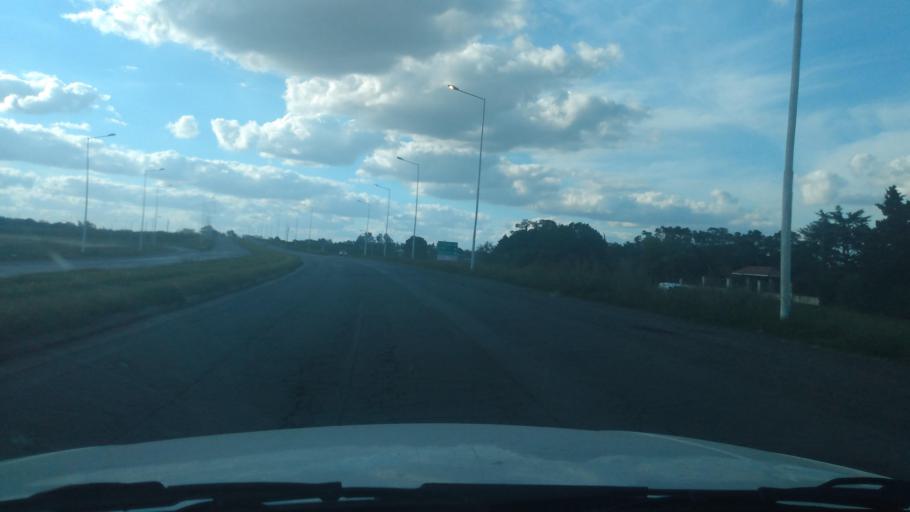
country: AR
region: Buenos Aires
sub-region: Partido de Mercedes
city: Mercedes
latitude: -34.6696
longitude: -59.3988
